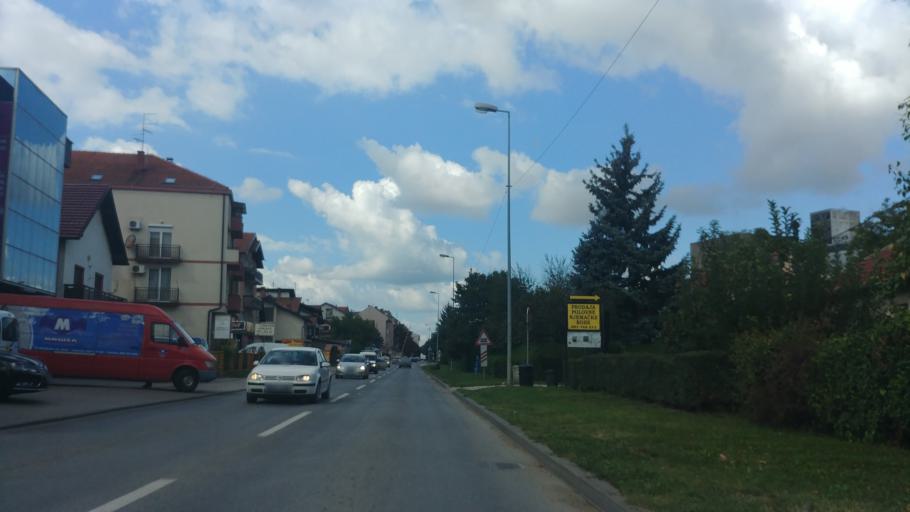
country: BA
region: Brcko
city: Brcko
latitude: 44.8681
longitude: 18.8190
